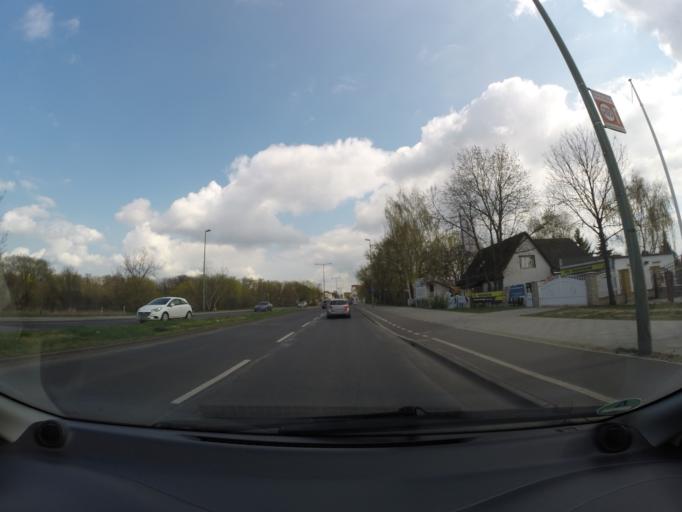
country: DE
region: Berlin
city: Mahlsdorf
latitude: 52.5195
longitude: 13.6247
